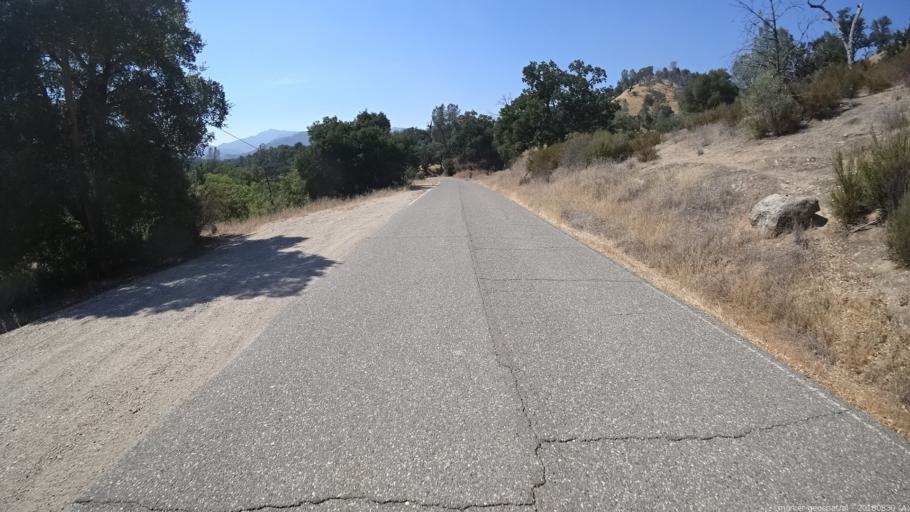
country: US
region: California
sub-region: Monterey County
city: King City
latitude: 36.0732
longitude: -121.3568
